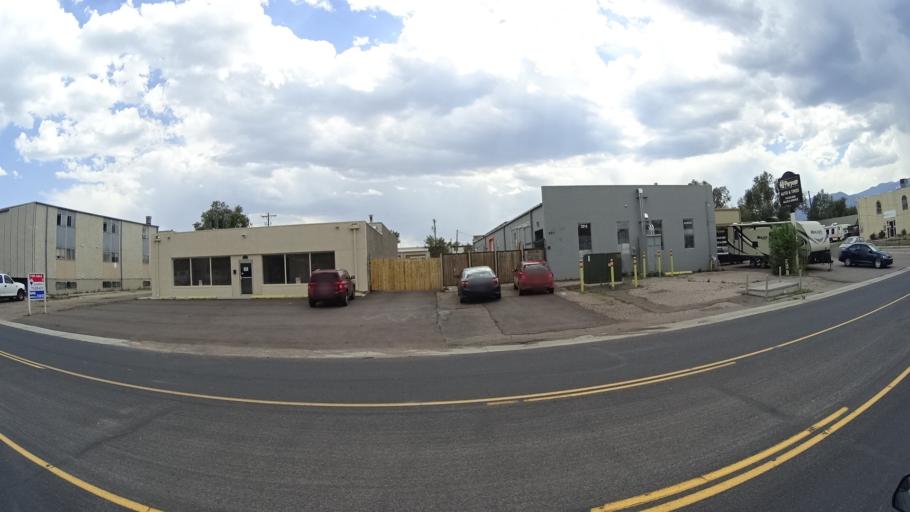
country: US
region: Colorado
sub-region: El Paso County
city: Colorado Springs
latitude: 38.8387
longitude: -104.7885
